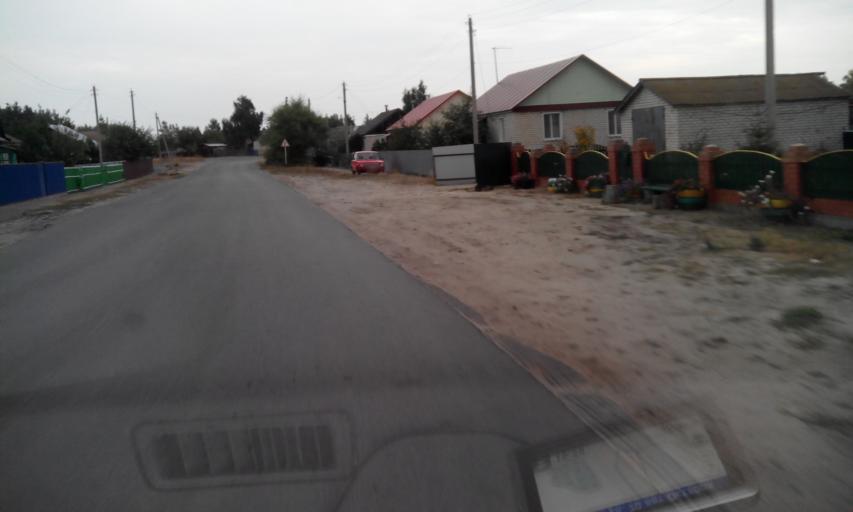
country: RU
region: Samara
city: Balasheyka
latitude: 53.1538
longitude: 48.1126
